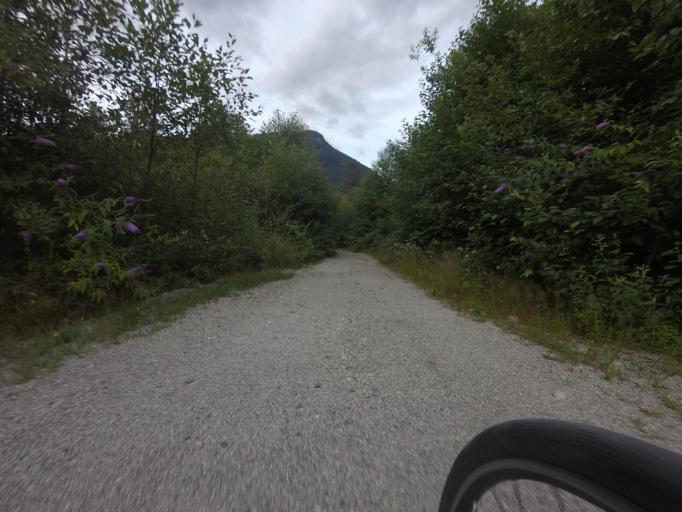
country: CA
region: British Columbia
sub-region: Greater Vancouver Regional District
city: Lions Bay
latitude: 49.5823
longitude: -123.2260
